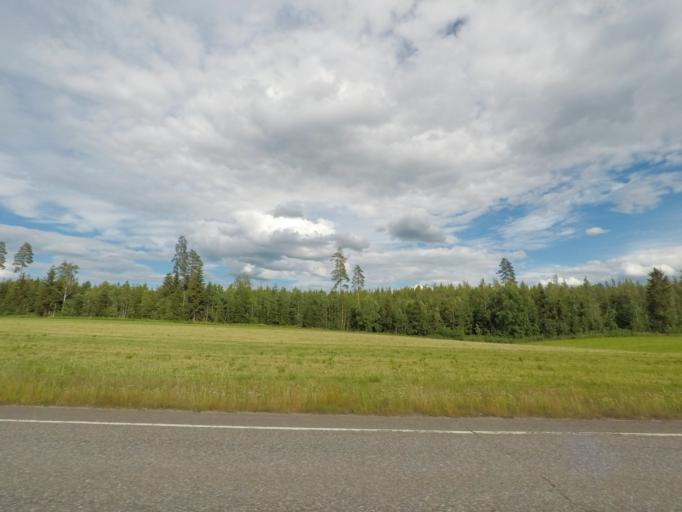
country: FI
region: Paijanne Tavastia
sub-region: Lahti
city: Hollola
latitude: 60.8277
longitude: 25.4891
